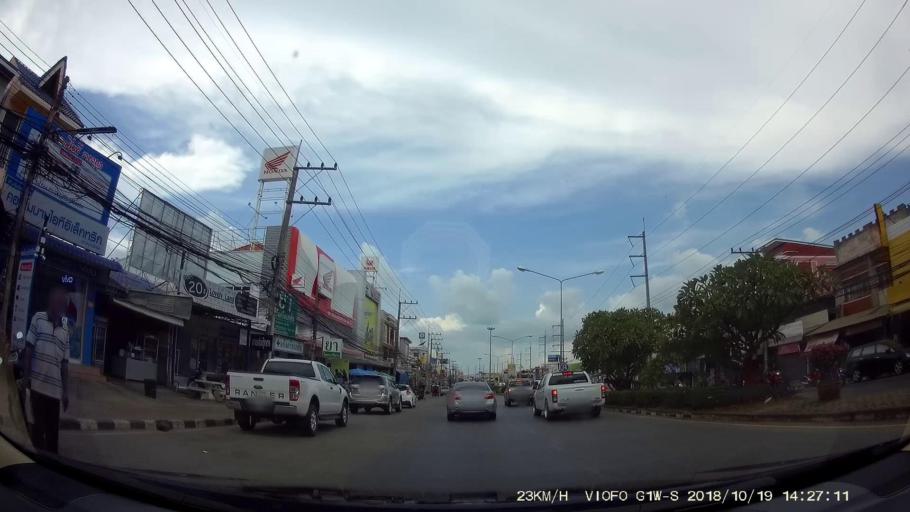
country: TH
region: Chaiyaphum
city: Kaeng Khro
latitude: 16.1103
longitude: 102.2584
